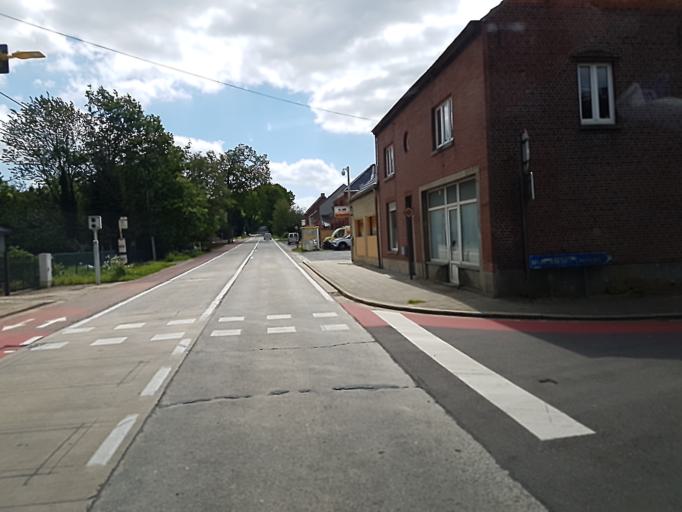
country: BE
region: Flanders
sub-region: Provincie Vlaams-Brabant
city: Diest
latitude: 51.0050
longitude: 5.0275
